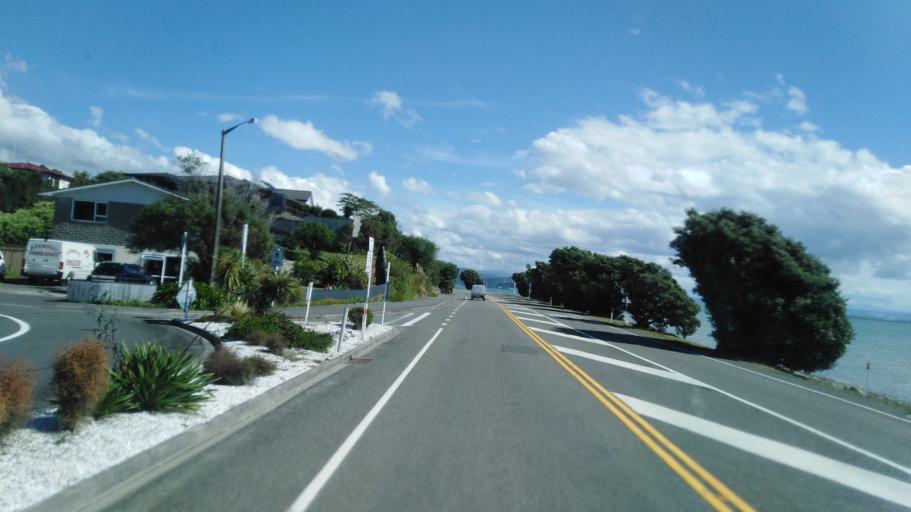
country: NZ
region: Nelson
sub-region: Nelson City
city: Nelson
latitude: -41.2253
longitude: 173.3209
